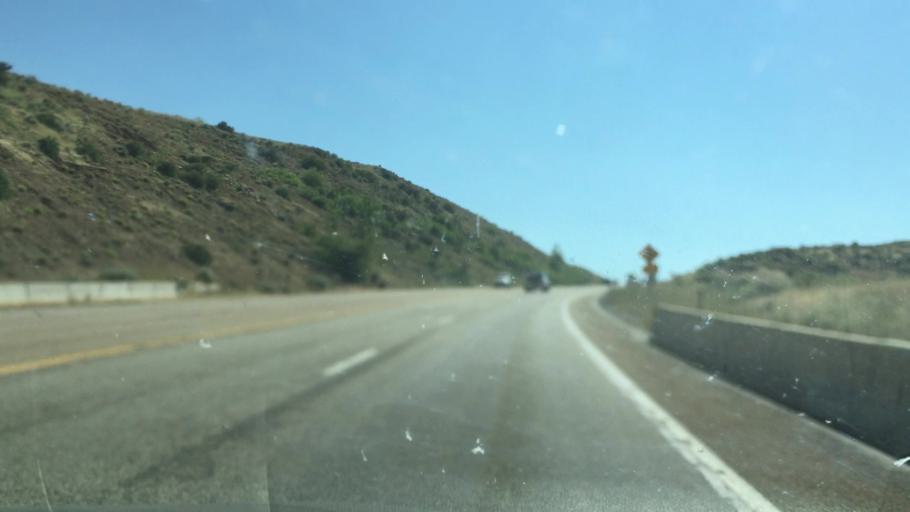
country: US
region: Idaho
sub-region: Ada County
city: Eagle
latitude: 43.8398
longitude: -116.2386
